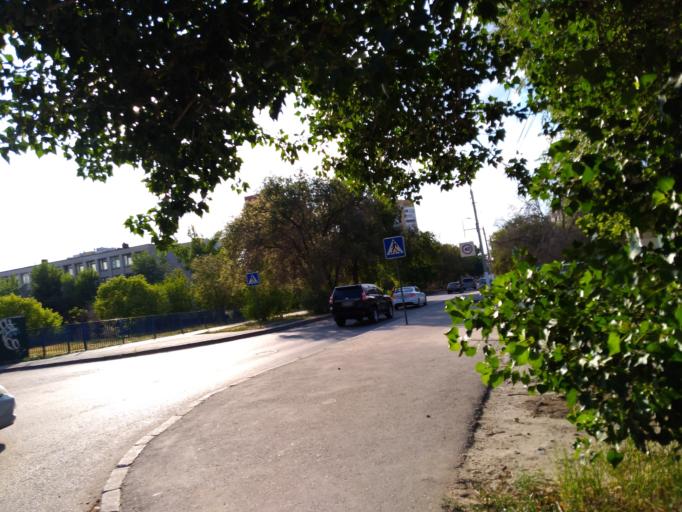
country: RU
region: Volgograd
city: Volgograd
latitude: 48.7201
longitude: 44.5145
